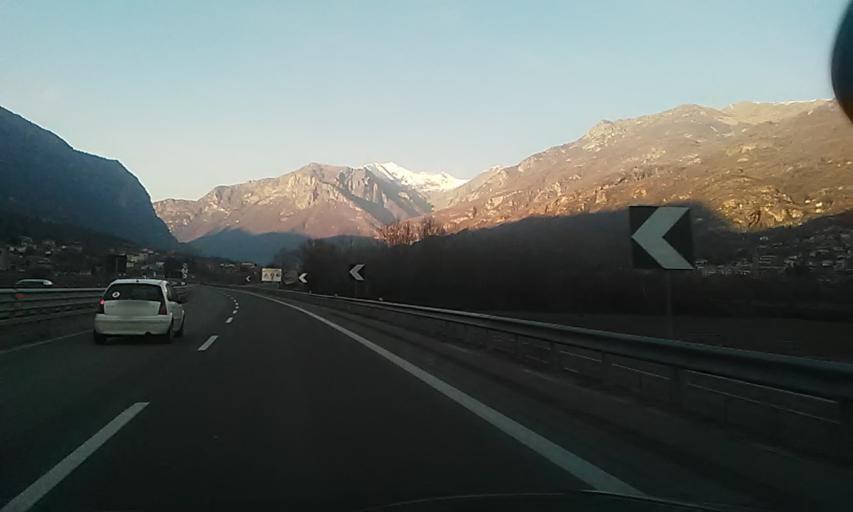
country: IT
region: Piedmont
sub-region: Provincia di Torino
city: Tavagnasco
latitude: 45.5391
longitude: 7.8287
